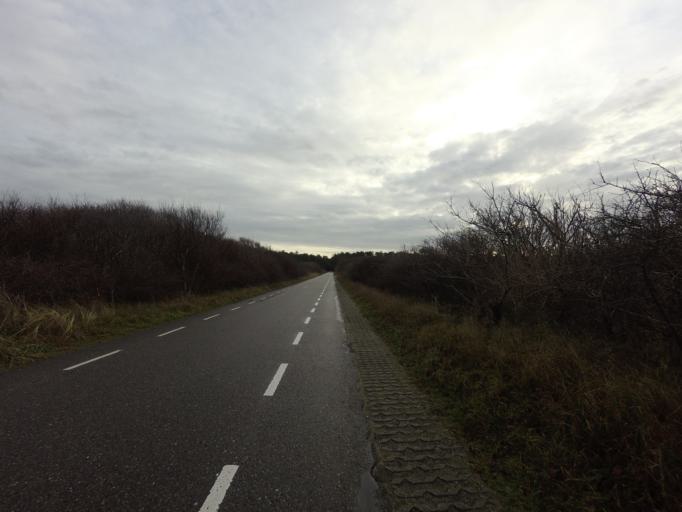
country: NL
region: North Holland
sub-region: Gemeente Texel
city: Den Burg
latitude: 53.0561
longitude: 4.7312
